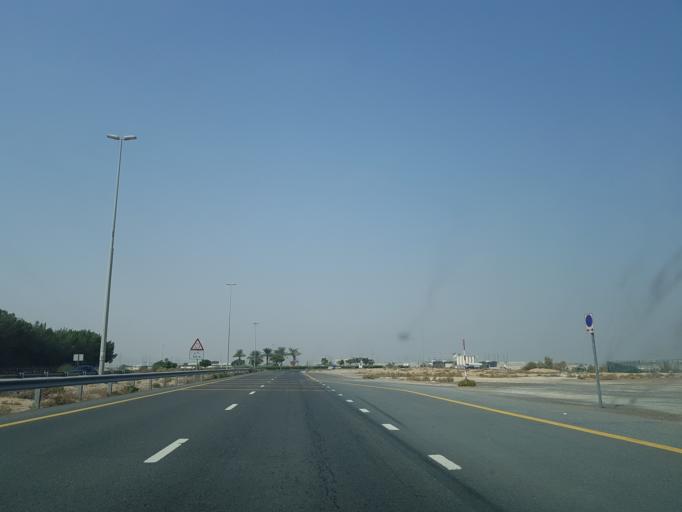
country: AE
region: Ash Shariqah
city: Sharjah
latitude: 25.1586
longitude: 55.4539
